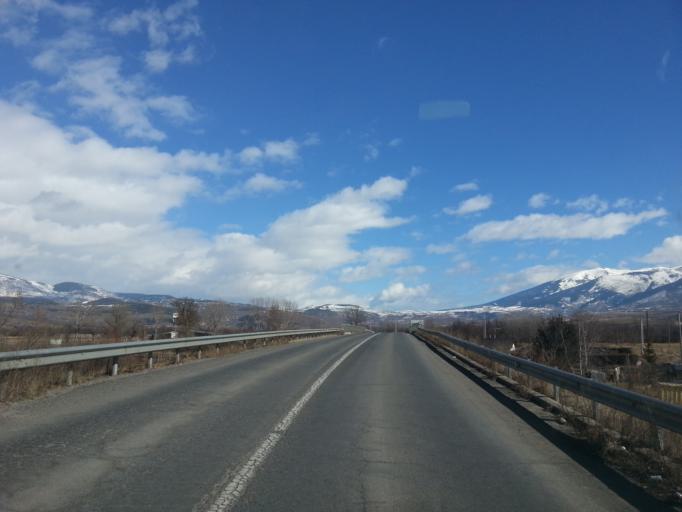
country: FR
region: Languedoc-Roussillon
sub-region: Departement des Pyrenees-Orientales
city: la Guingueta d'Ix
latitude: 42.4451
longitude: 1.9429
